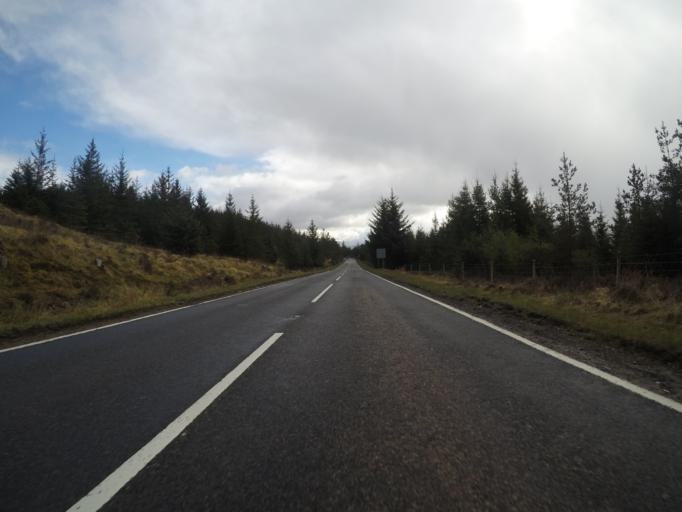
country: GB
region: Scotland
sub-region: Highland
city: Spean Bridge
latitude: 57.0819
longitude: -4.9459
